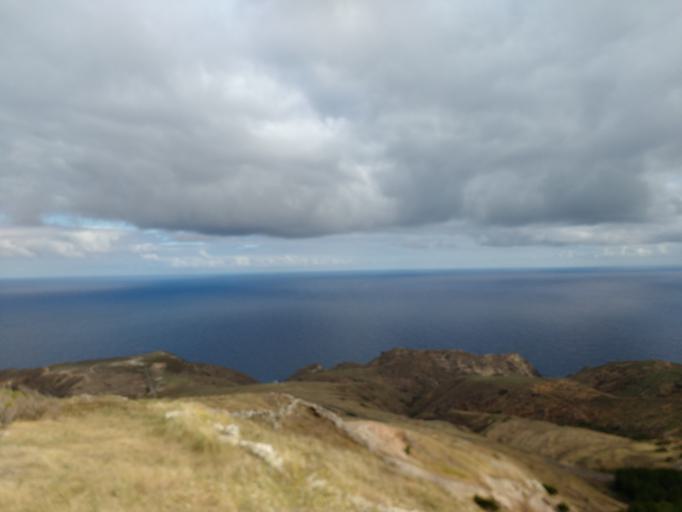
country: PT
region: Madeira
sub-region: Porto Santo
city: Camacha
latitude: 33.0869
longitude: -16.3272
